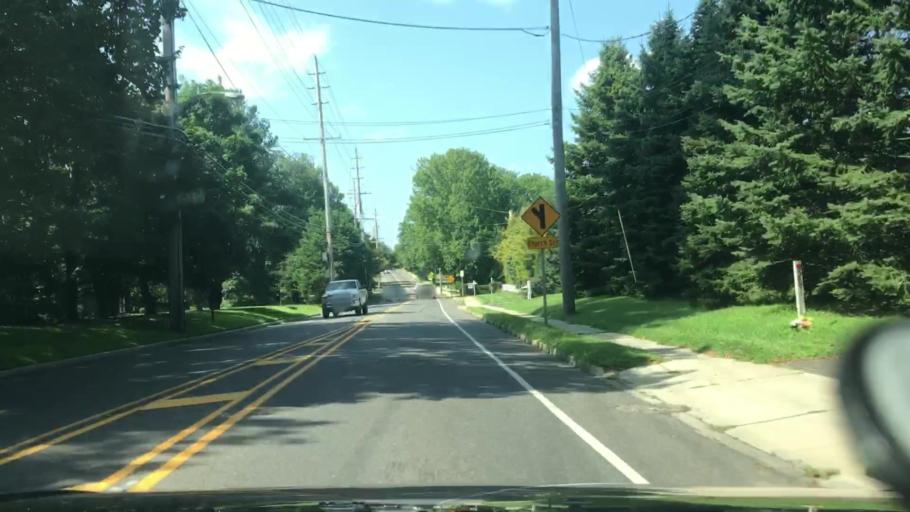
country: US
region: New Jersey
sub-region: Monmouth County
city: Little Silver
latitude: 40.3437
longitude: -74.0380
